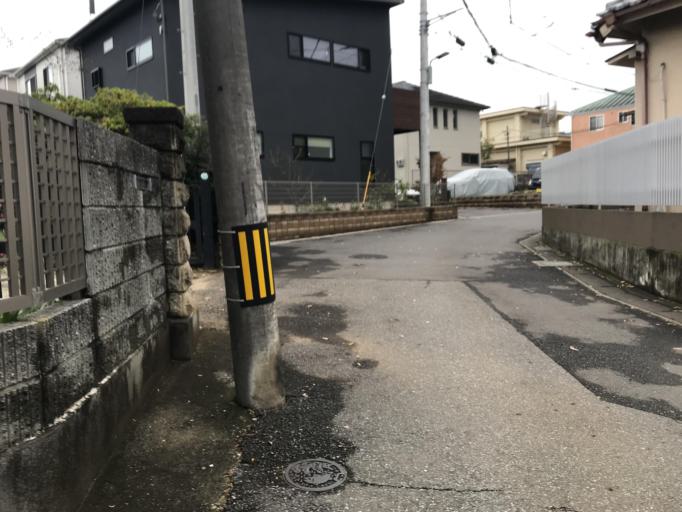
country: JP
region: Chiba
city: Matsudo
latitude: 35.7483
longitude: 139.9003
